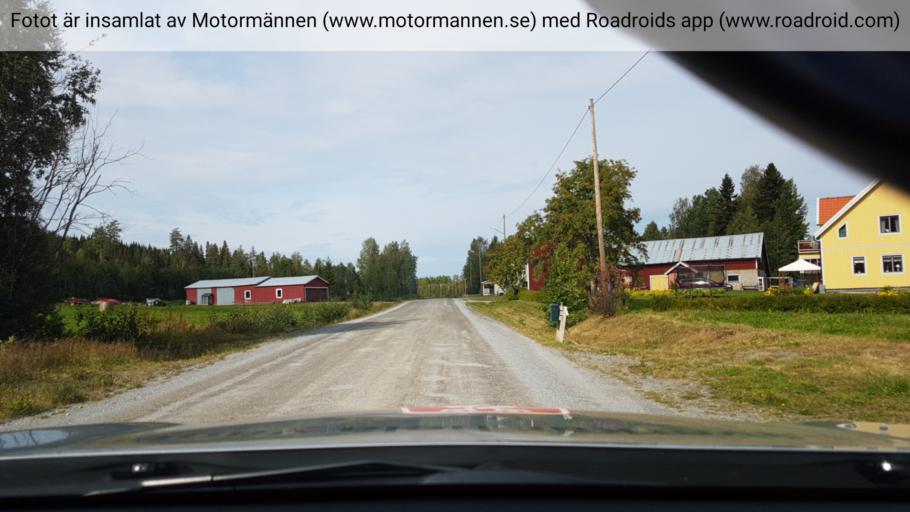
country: SE
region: Vaesterbotten
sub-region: Bjurholms Kommun
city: Bjurholm
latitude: 63.8680
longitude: 19.4606
